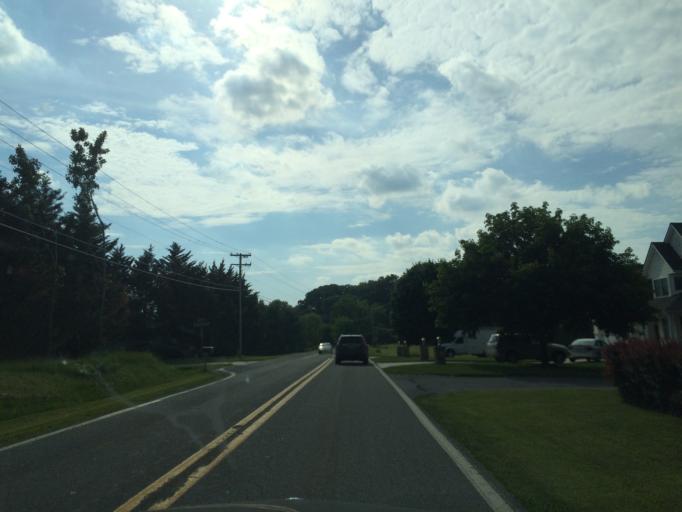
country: US
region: Maryland
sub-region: Carroll County
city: Eldersburg
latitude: 39.4825
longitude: -76.9215
